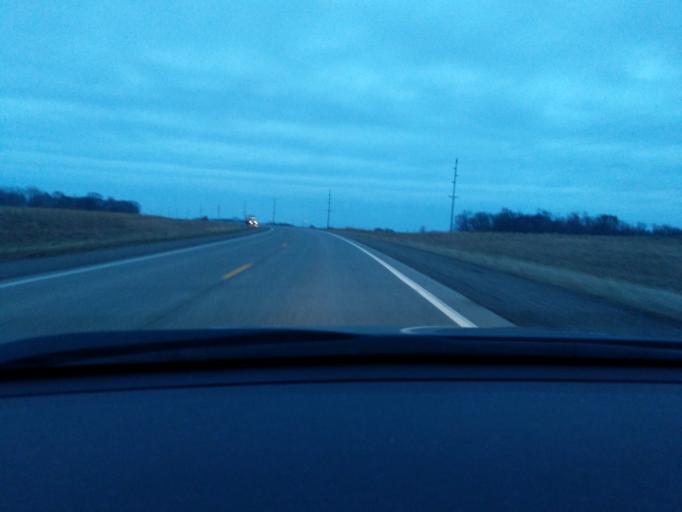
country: US
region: Minnesota
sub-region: Yellow Medicine County
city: Granite Falls
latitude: 44.7895
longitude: -95.4479
